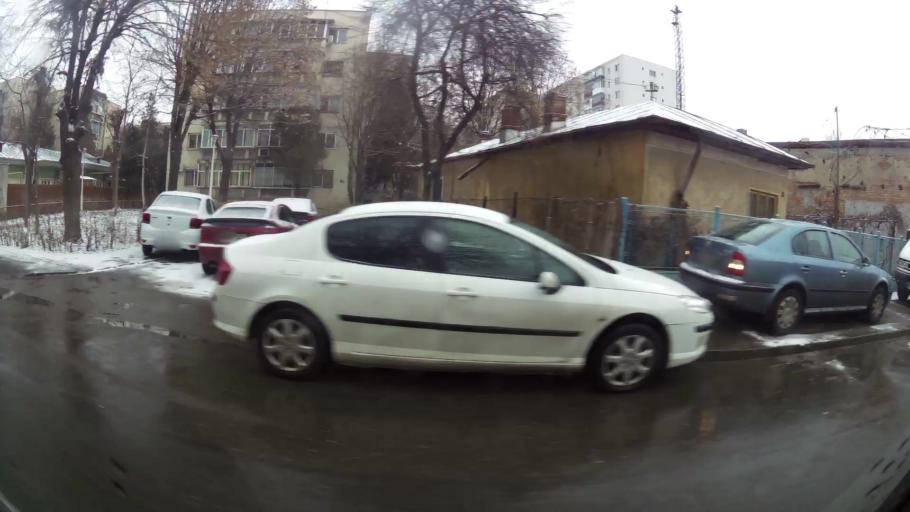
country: RO
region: Prahova
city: Ploiesti
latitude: 44.9268
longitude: 26.0246
